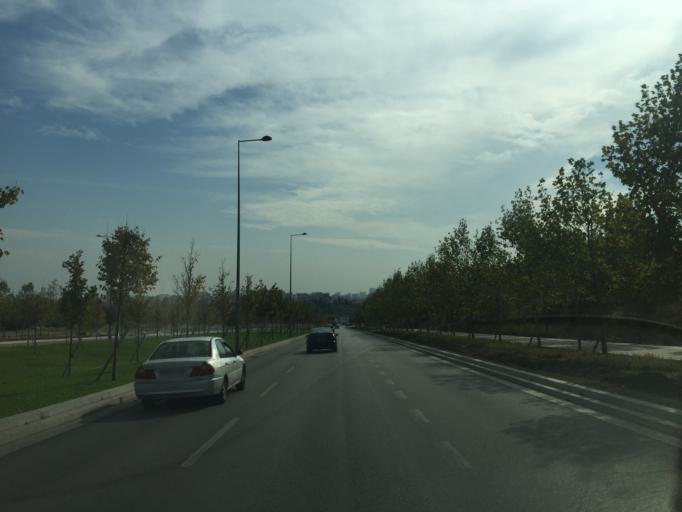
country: PT
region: Lisbon
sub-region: Odivelas
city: Olival do Basto
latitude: 38.7666
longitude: -9.1487
